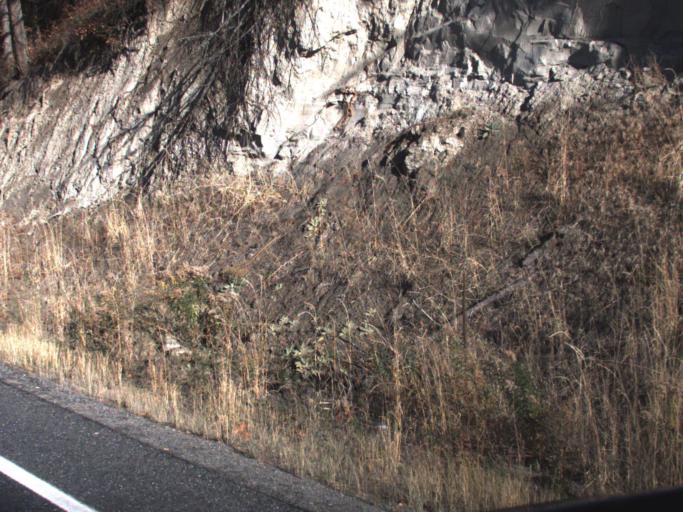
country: US
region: Washington
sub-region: Stevens County
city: Kettle Falls
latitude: 48.6185
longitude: -118.0734
